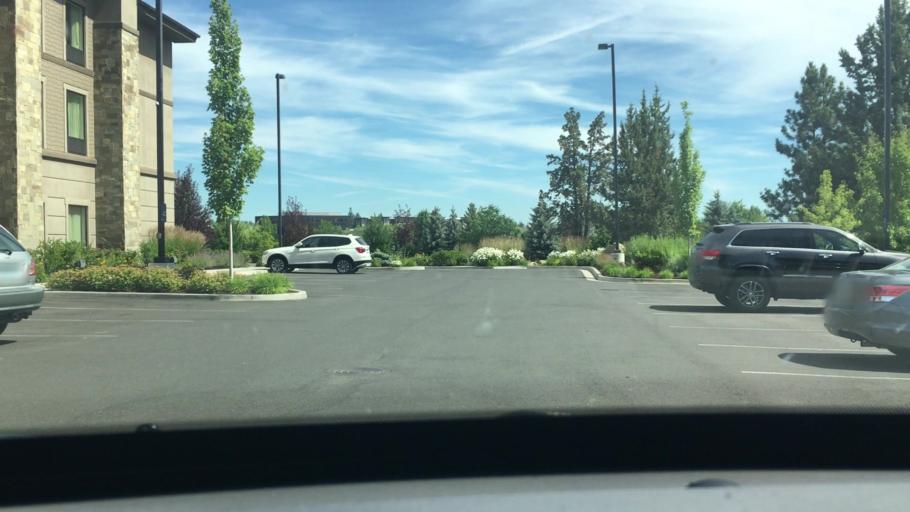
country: US
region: Oregon
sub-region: Deschutes County
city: Bend
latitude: 44.0443
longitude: -121.3179
